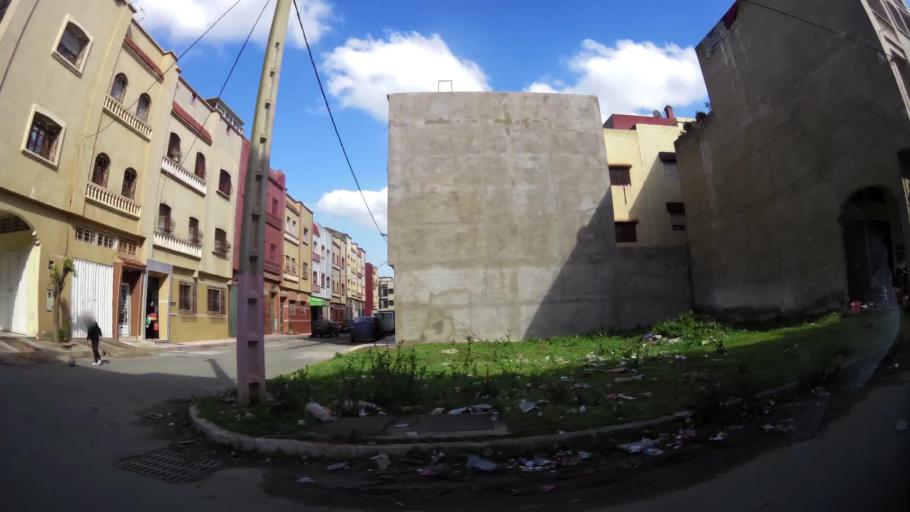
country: MA
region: Grand Casablanca
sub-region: Mediouna
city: Mediouna
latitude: 33.3840
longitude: -7.5319
